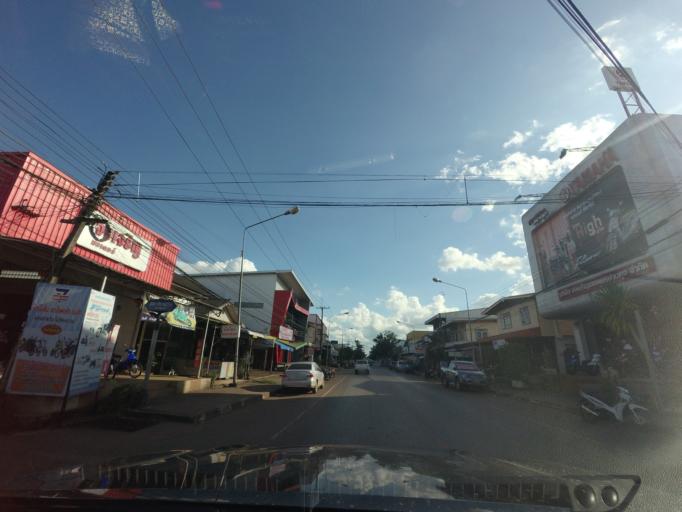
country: TH
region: Changwat Udon Thani
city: Ban Dung
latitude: 17.6964
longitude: 103.2588
